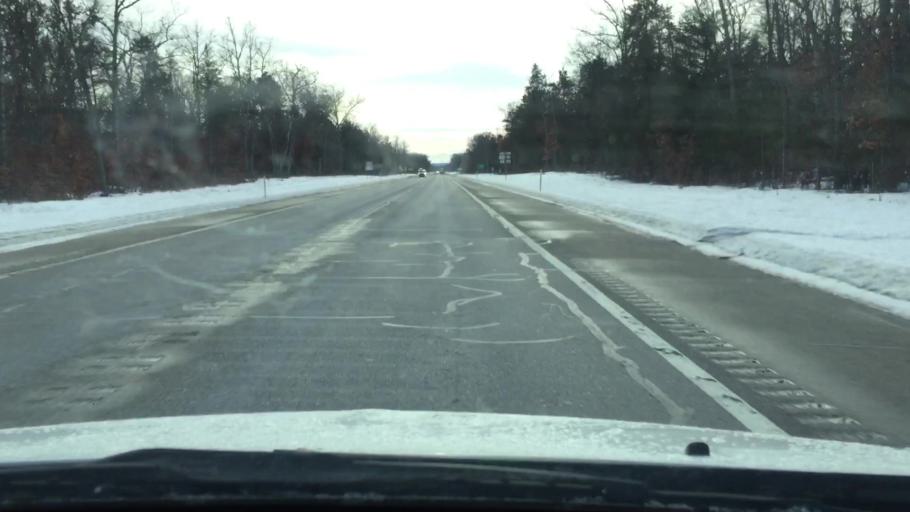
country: US
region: Michigan
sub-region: Wexford County
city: Manton
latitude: 44.5268
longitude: -85.3883
